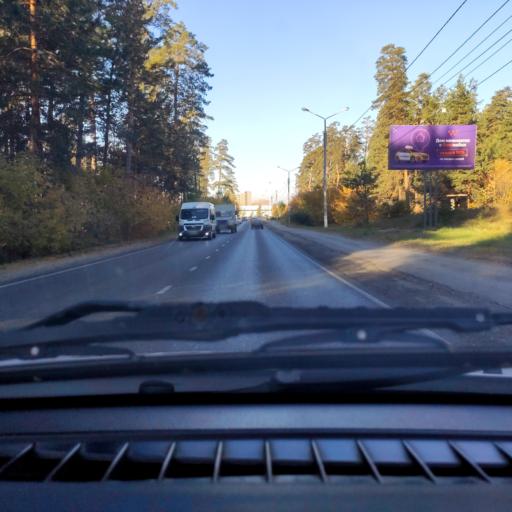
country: RU
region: Samara
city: Tol'yatti
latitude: 53.4762
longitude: 49.3305
